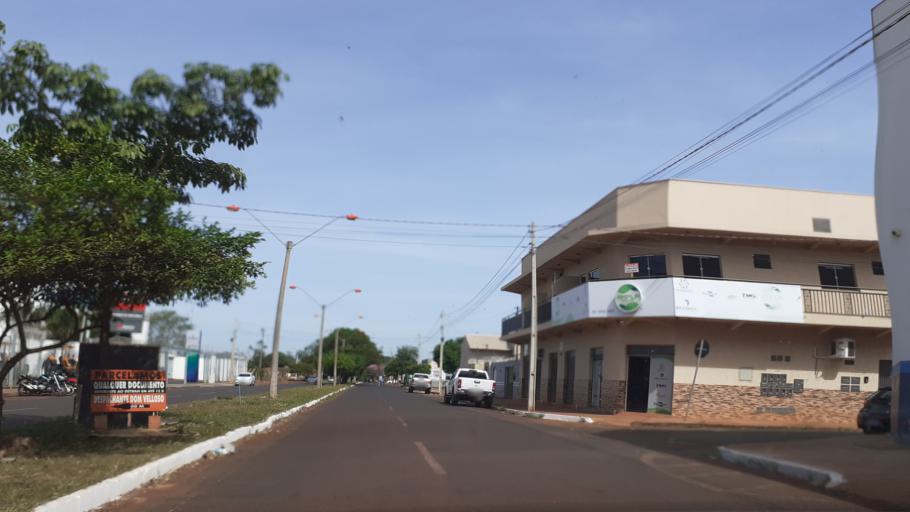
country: BR
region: Goias
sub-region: Itumbiara
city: Itumbiara
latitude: -18.4098
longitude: -49.2562
